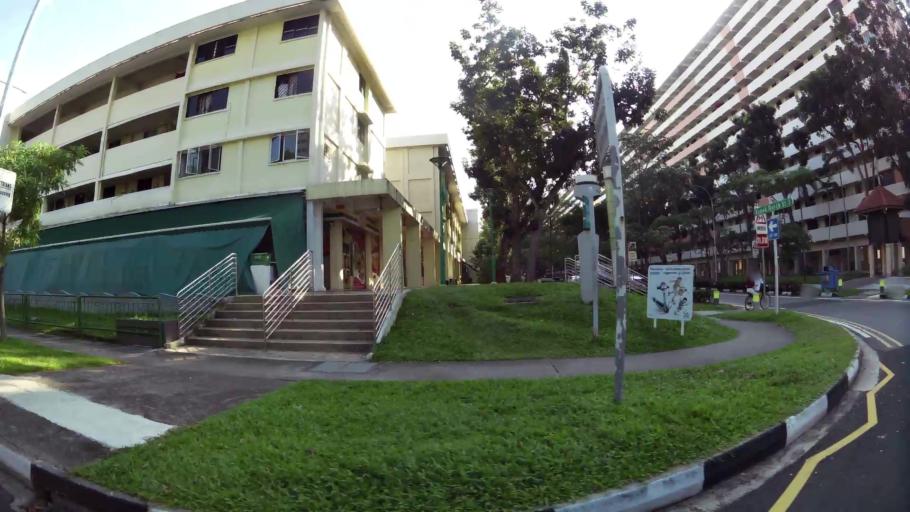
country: SG
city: Singapore
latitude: 1.3319
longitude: 103.9304
